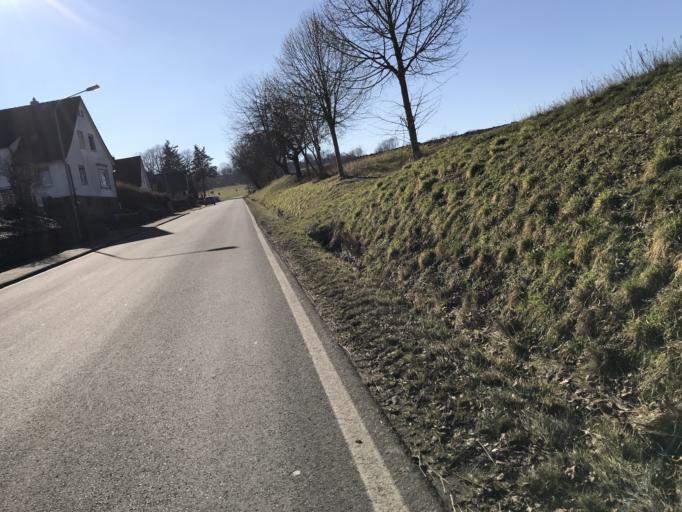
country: DE
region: Hesse
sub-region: Regierungsbezirk Giessen
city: Rabenau
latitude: 50.6600
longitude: 8.8888
